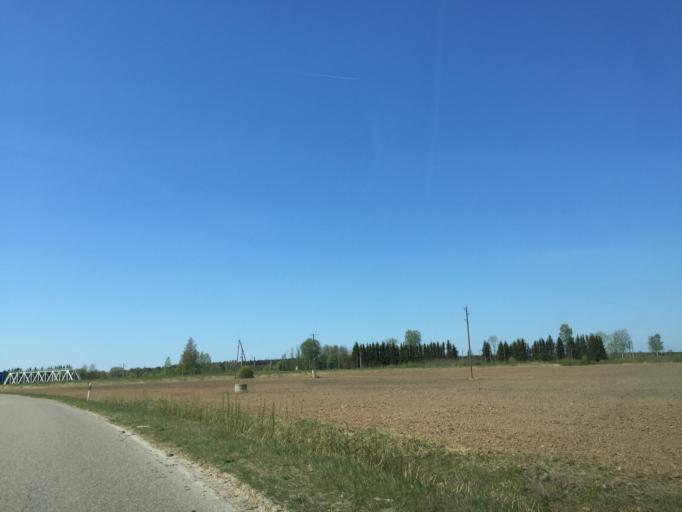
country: LV
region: Saulkrastu
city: Saulkrasti
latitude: 57.3300
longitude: 24.4644
